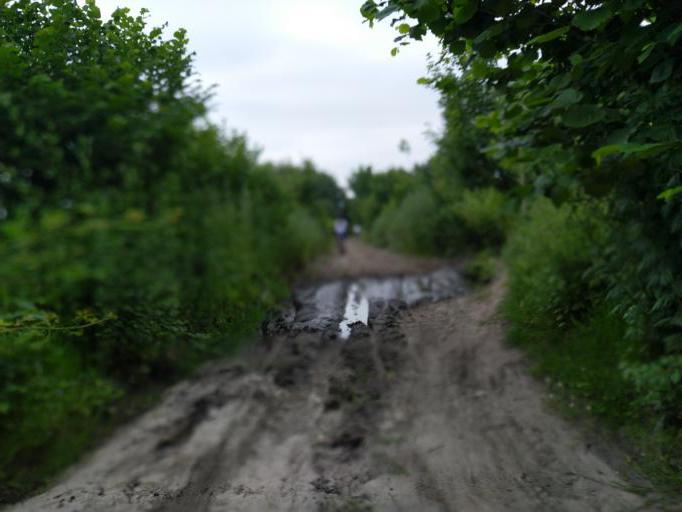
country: BE
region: Wallonia
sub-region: Province du Hainaut
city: Jurbise
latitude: 50.4891
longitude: 3.8877
